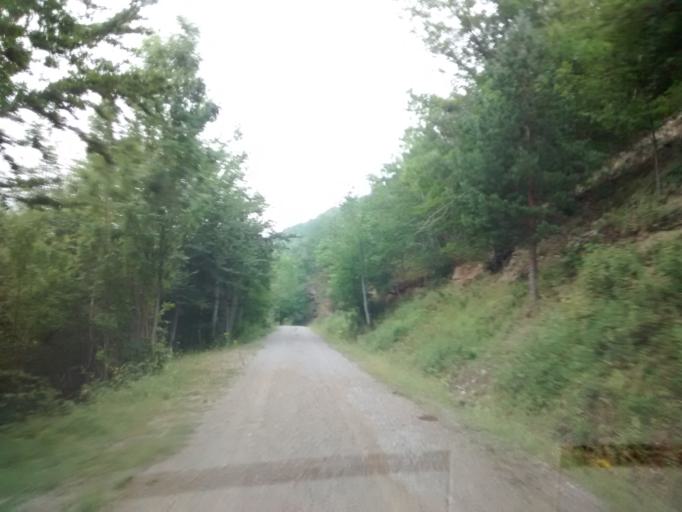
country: ES
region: La Rioja
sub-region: Provincia de La Rioja
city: Ajamil
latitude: 42.1485
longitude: -2.4798
